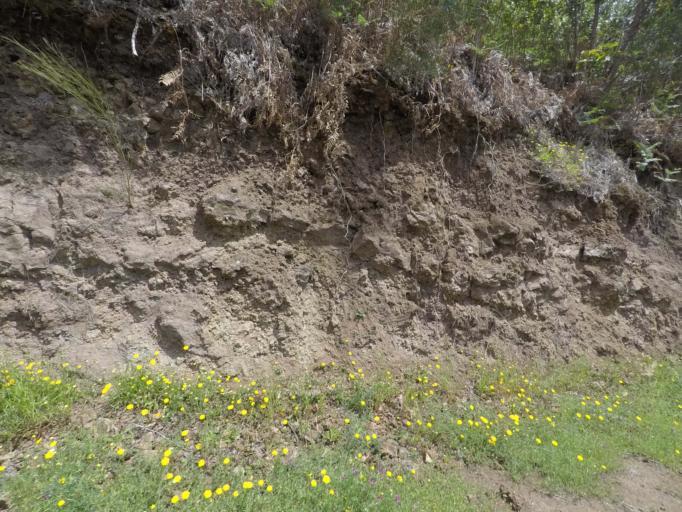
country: PT
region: Madeira
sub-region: Calheta
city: Estreito da Calheta
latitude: 32.7463
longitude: -17.1950
